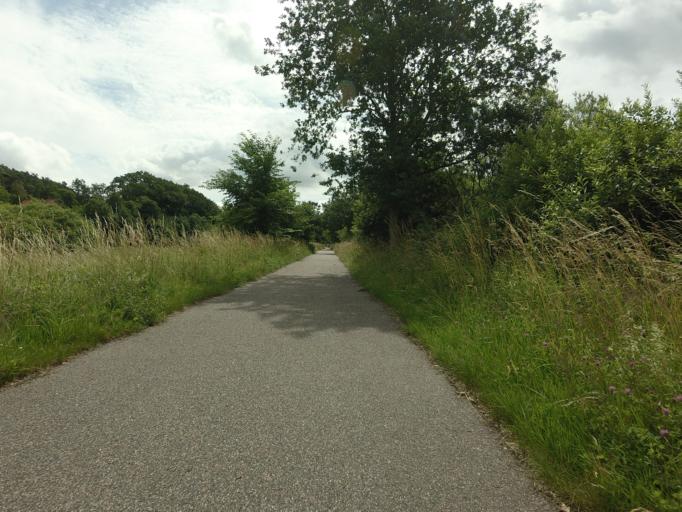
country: DK
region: Central Jutland
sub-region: Randers Kommune
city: Langa
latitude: 56.3707
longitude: 9.8994
